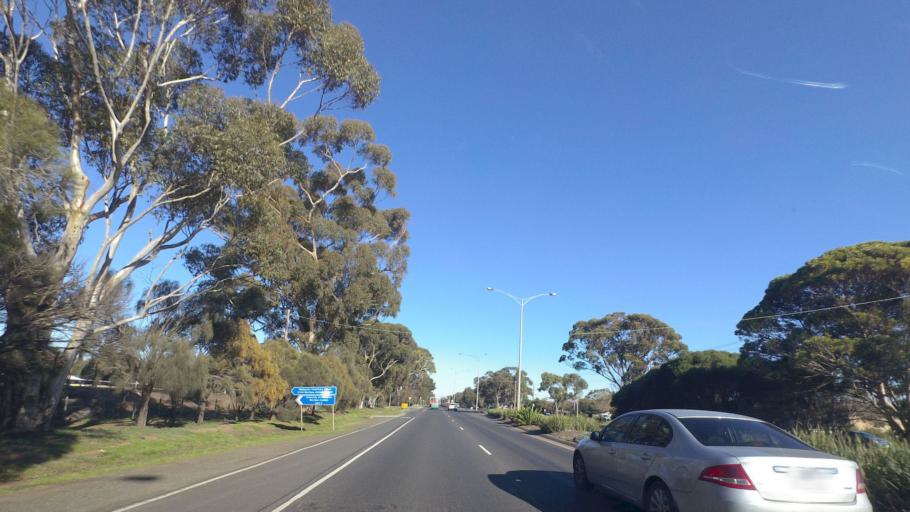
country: AU
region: Victoria
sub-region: Wyndham
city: Hoppers Crossing
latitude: -37.8884
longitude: 144.6926
